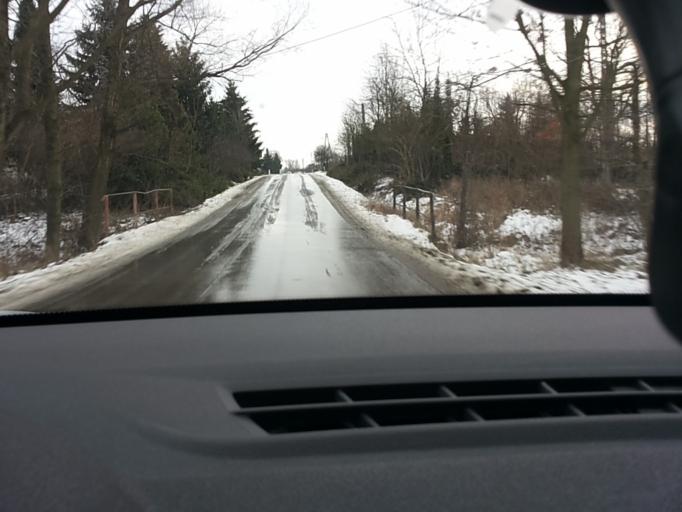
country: PL
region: Lodz Voivodeship
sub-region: Powiat skierniewicki
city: Makow
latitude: 51.9891
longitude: 20.0888
